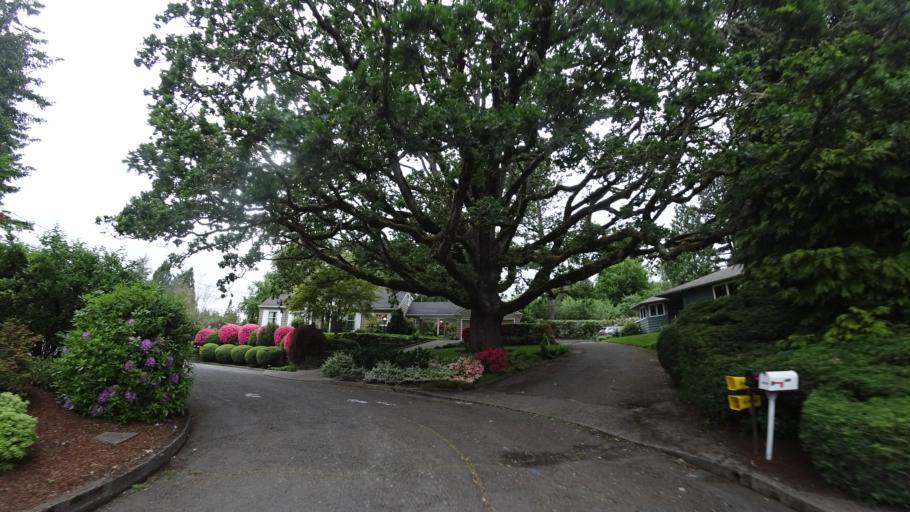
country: US
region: Oregon
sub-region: Multnomah County
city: Portland
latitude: 45.4893
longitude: -122.7074
